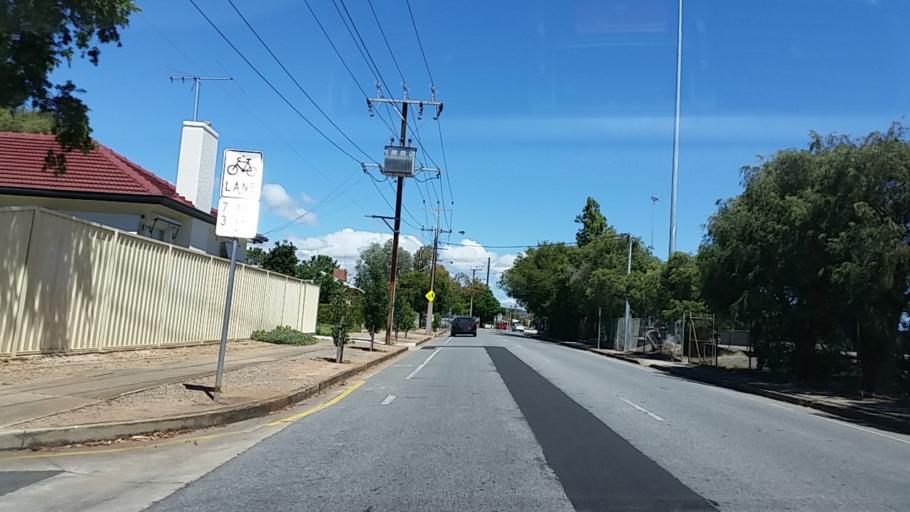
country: AU
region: South Australia
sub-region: Marion
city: South Plympton
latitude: -34.9809
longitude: 138.5651
